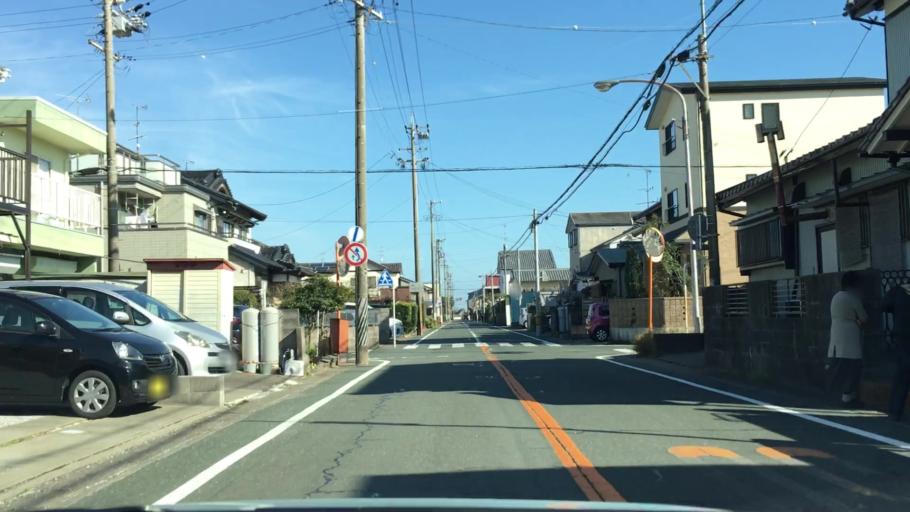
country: JP
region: Shizuoka
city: Kosai-shi
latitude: 34.6956
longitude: 137.6037
